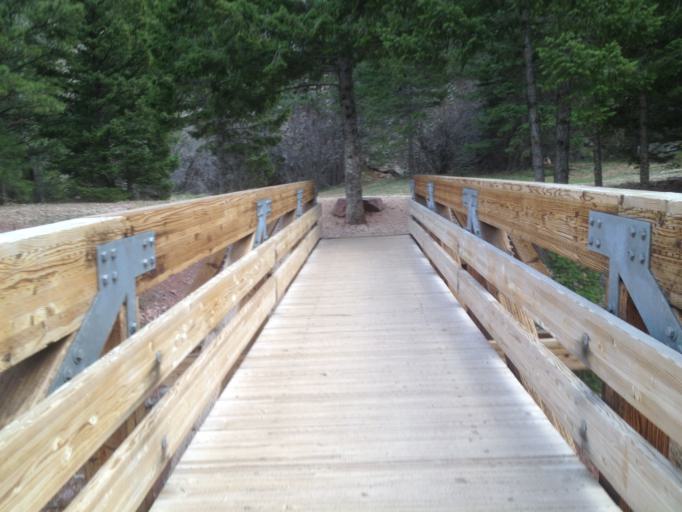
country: US
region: Colorado
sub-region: Boulder County
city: Coal Creek
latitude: 39.9276
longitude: -105.2918
